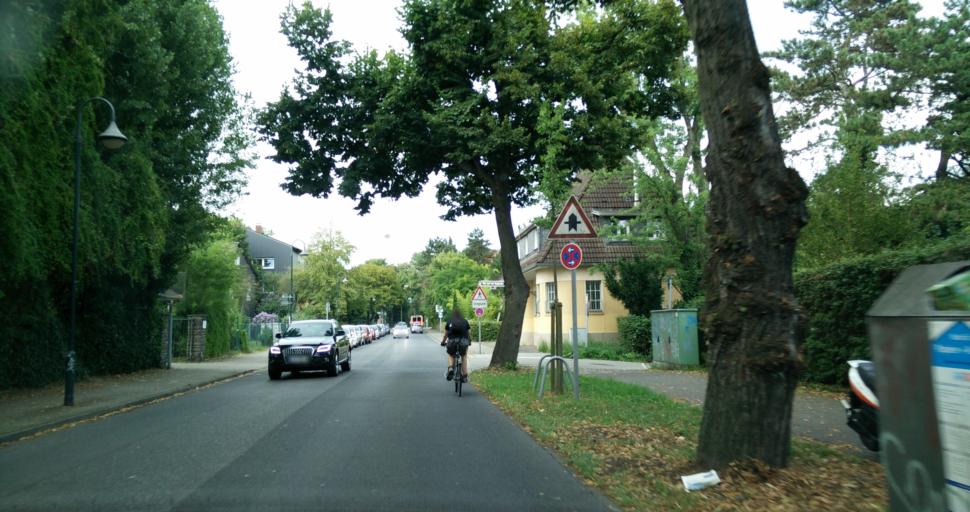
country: DE
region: North Rhine-Westphalia
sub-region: Regierungsbezirk Dusseldorf
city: Meerbusch
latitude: 51.2975
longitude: 6.7419
